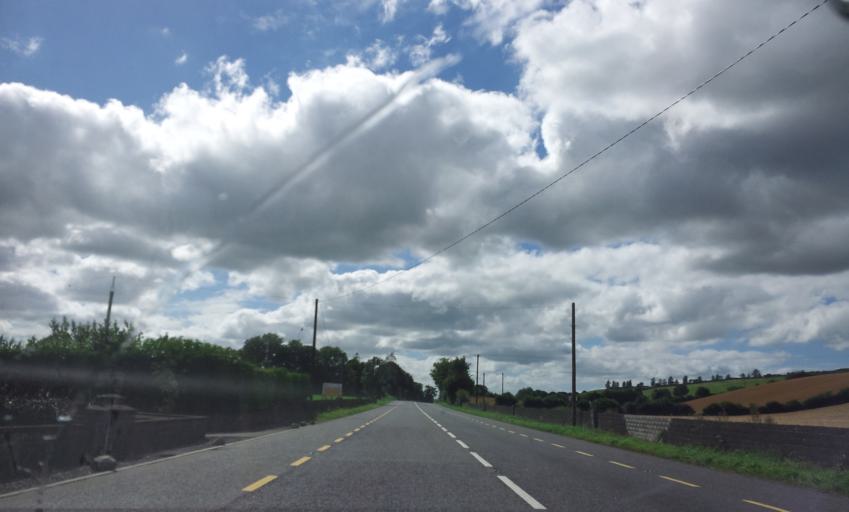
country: IE
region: Munster
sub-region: County Cork
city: Killumney
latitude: 51.8780
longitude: -8.6961
